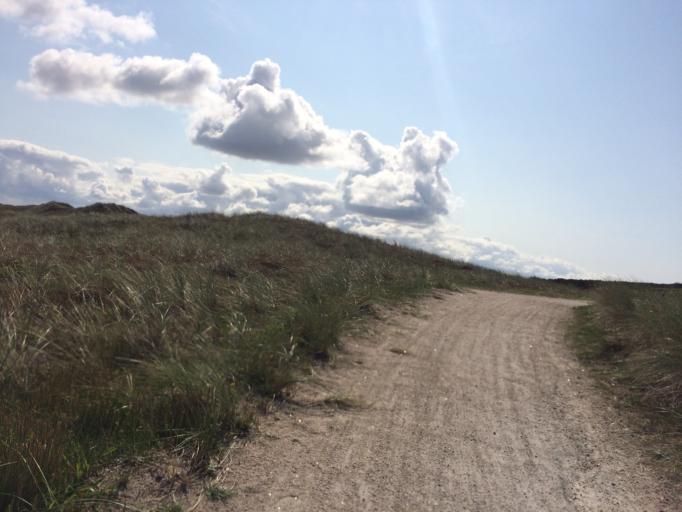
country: DK
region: Central Jutland
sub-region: Ringkobing-Skjern Kommune
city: Hvide Sande
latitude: 55.9404
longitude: 8.1491
